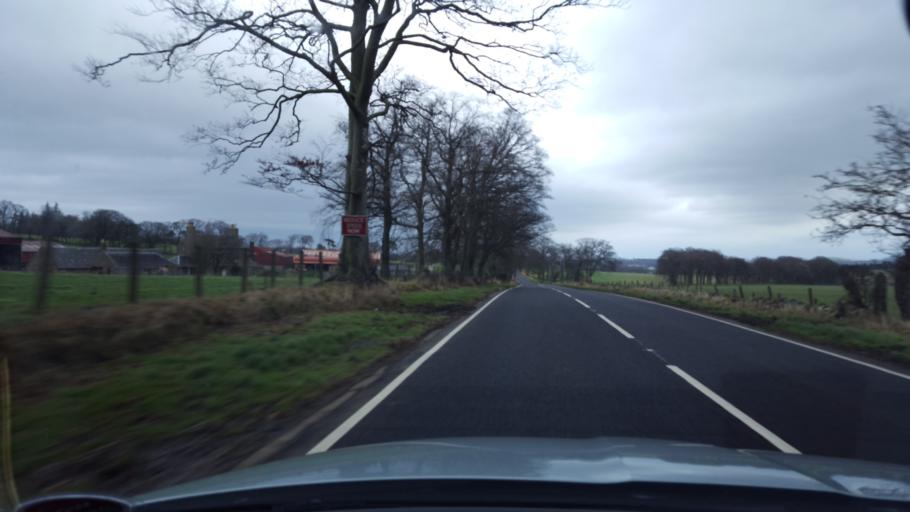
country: GB
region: Scotland
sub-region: West Lothian
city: Kirknewton
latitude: 55.8557
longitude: -3.4286
